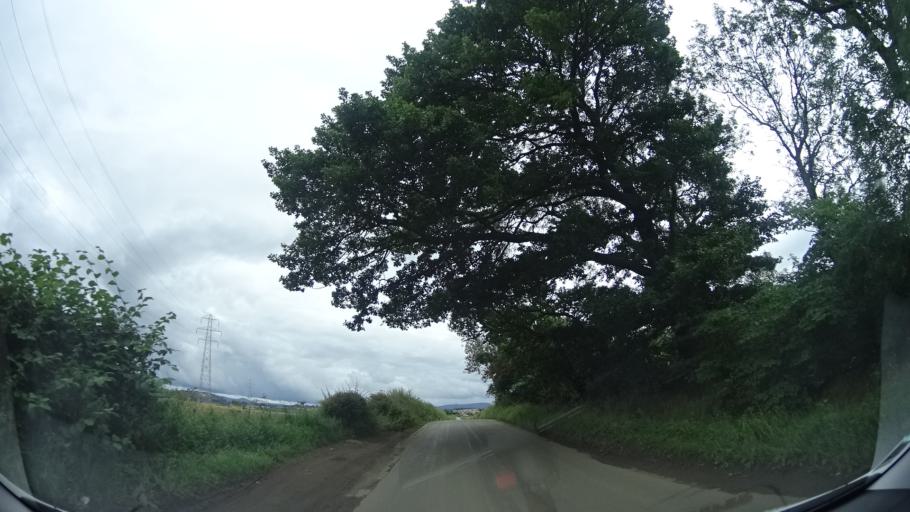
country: GB
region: Scotland
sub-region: West Lothian
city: Kirknewton
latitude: 55.9057
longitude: -3.4358
